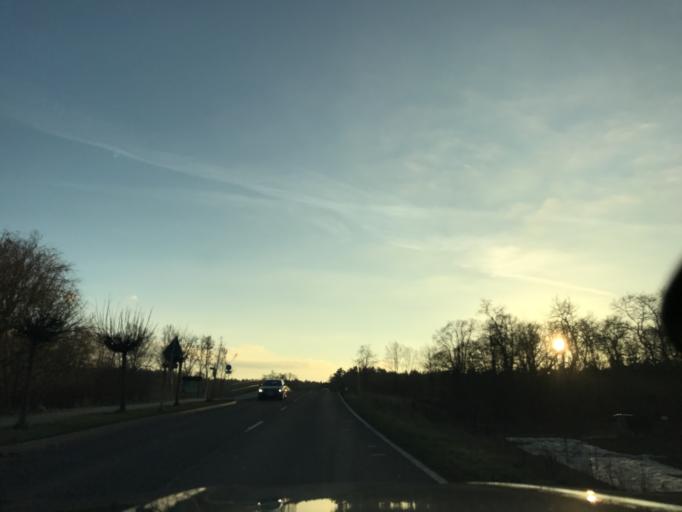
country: DE
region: Saxony-Anhalt
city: Genthin
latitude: 52.4232
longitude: 12.2070
